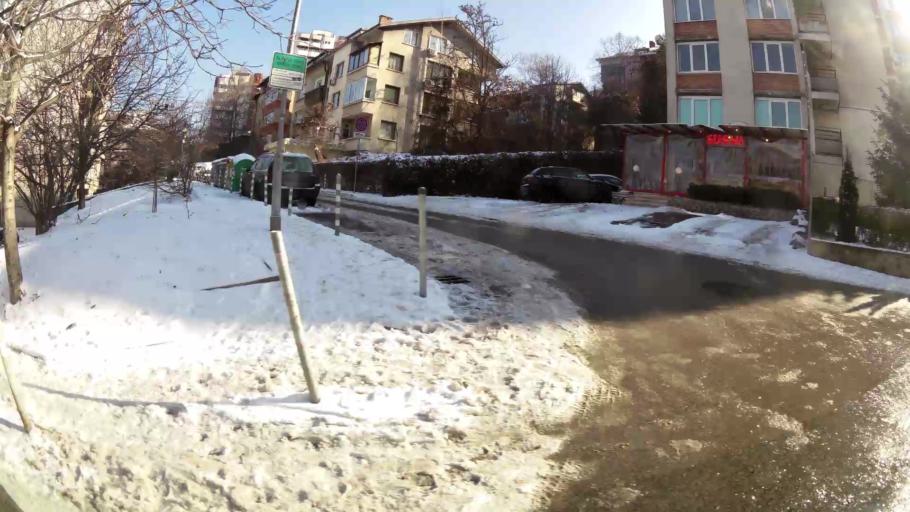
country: BG
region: Sofia-Capital
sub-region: Stolichna Obshtina
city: Sofia
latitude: 42.6724
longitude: 23.3139
